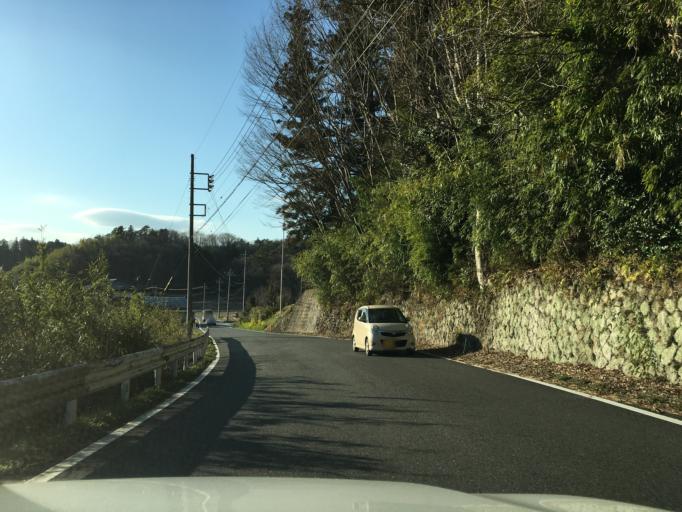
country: JP
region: Ibaraki
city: Daigo
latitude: 36.7742
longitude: 140.2491
